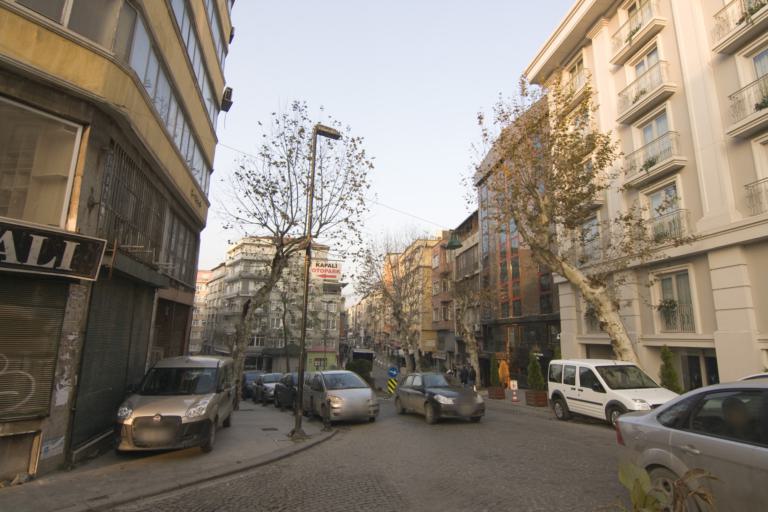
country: TR
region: Istanbul
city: Eminoenue
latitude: 41.0069
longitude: 28.9715
